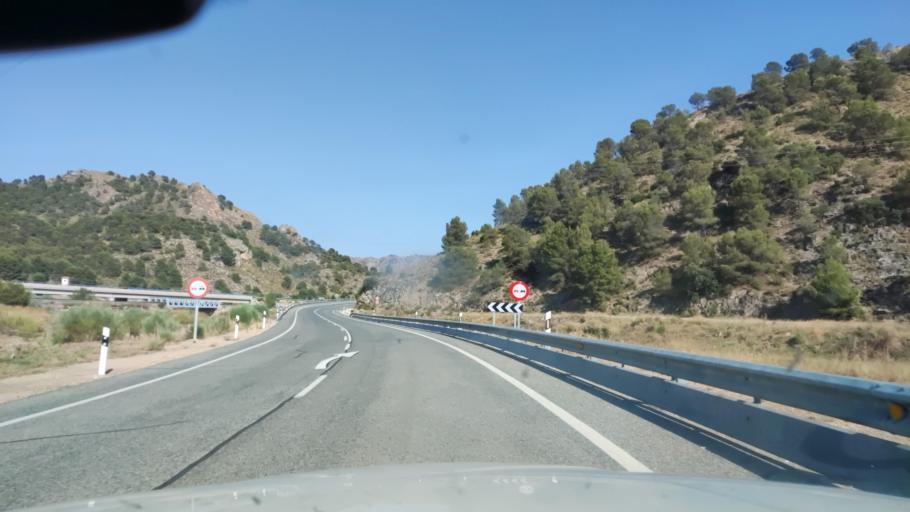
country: ES
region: Castille-La Mancha
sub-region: Provincia de Albacete
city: Tobarra
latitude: 38.6711
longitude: -1.6698
